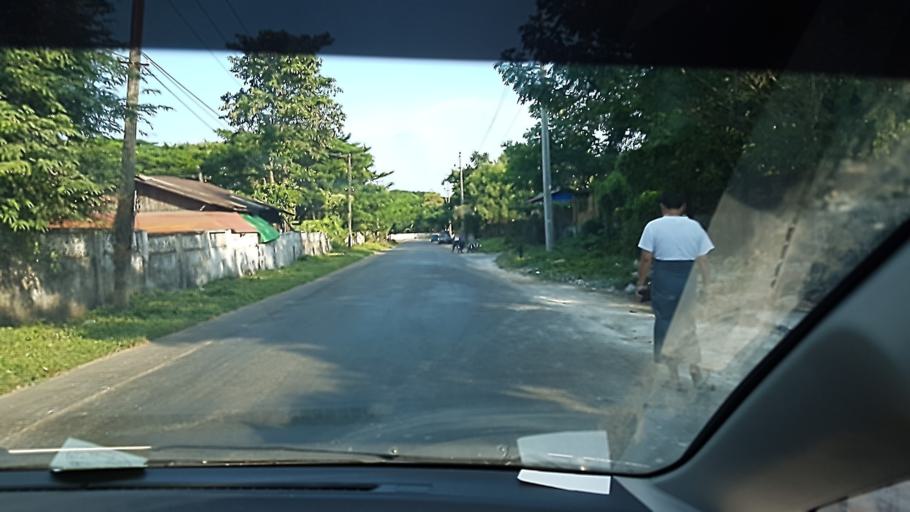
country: MM
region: Yangon
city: Yangon
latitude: 16.8132
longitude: 96.1635
